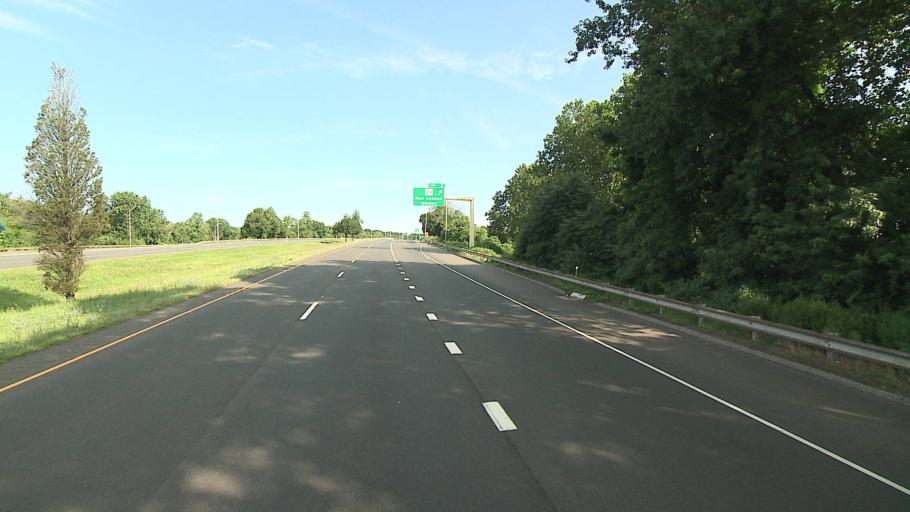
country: US
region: Connecticut
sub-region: Fairfield County
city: Norwalk
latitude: 41.1241
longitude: -73.4246
